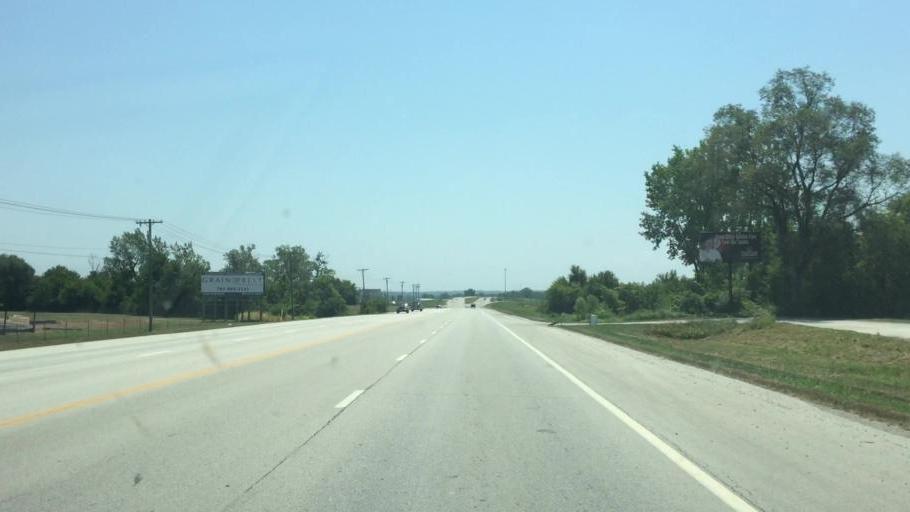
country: US
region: Kansas
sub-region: Doniphan County
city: Wathena
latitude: 39.7540
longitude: -94.9357
